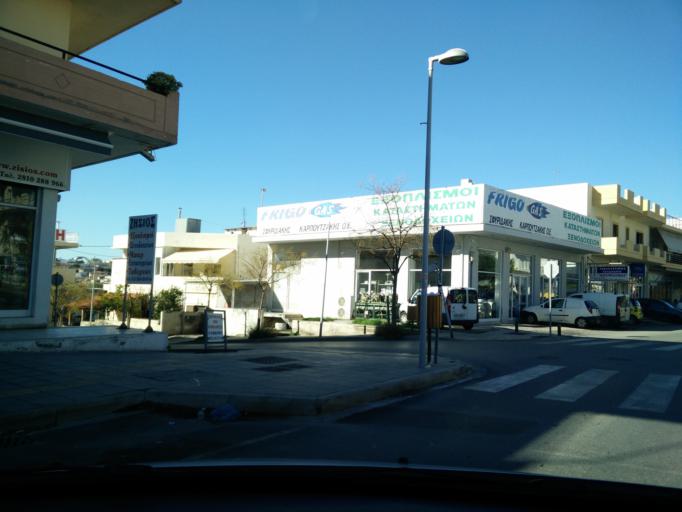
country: GR
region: Crete
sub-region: Nomos Irakleiou
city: Nea Alikarnassos
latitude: 35.3359
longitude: 25.1578
